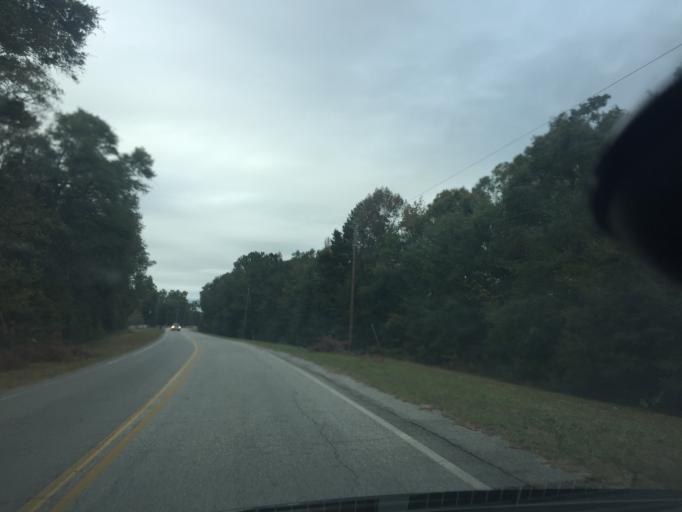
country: US
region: Georgia
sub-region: Chatham County
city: Bloomingdale
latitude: 32.1105
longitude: -81.3847
